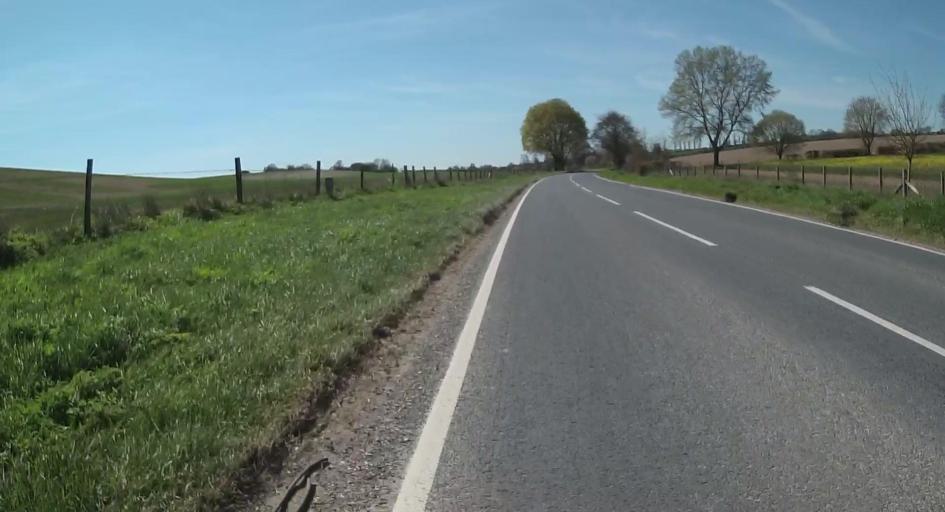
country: GB
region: England
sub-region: Hampshire
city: Chandlers Ford
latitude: 51.0948
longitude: -1.4201
